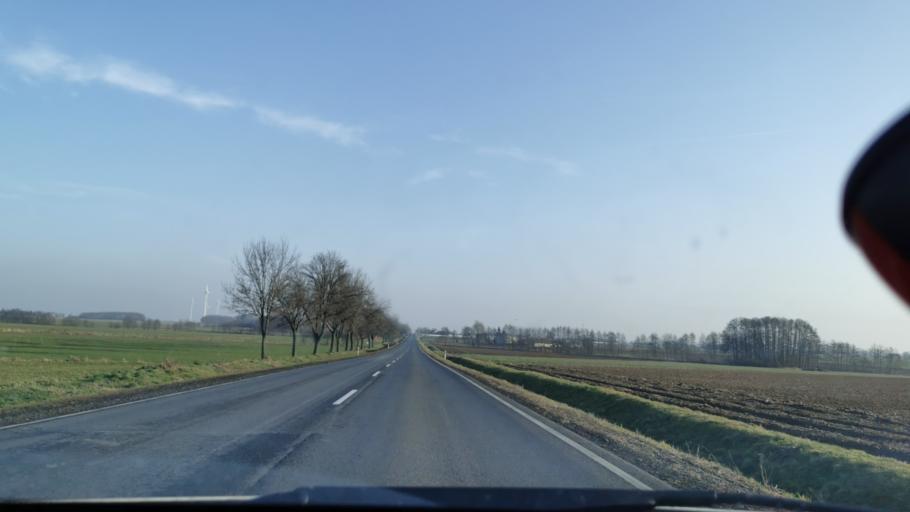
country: PL
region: Lodz Voivodeship
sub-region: Powiat sieradzki
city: Blaszki
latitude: 51.6791
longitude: 18.3475
